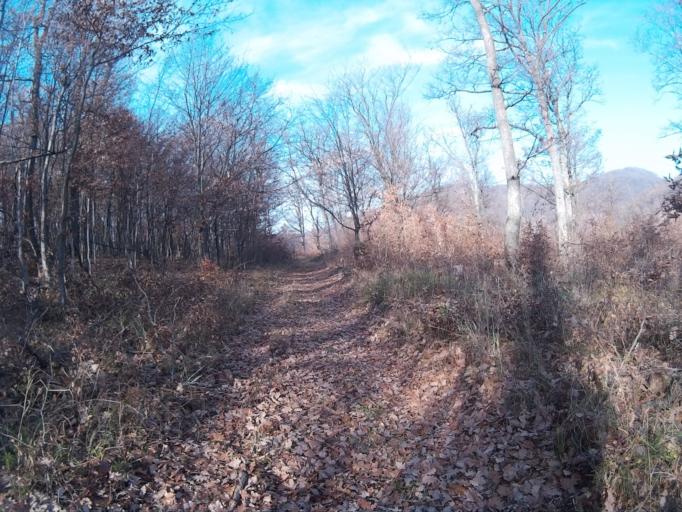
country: HU
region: Heves
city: Belapatfalva
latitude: 48.0360
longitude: 20.3904
